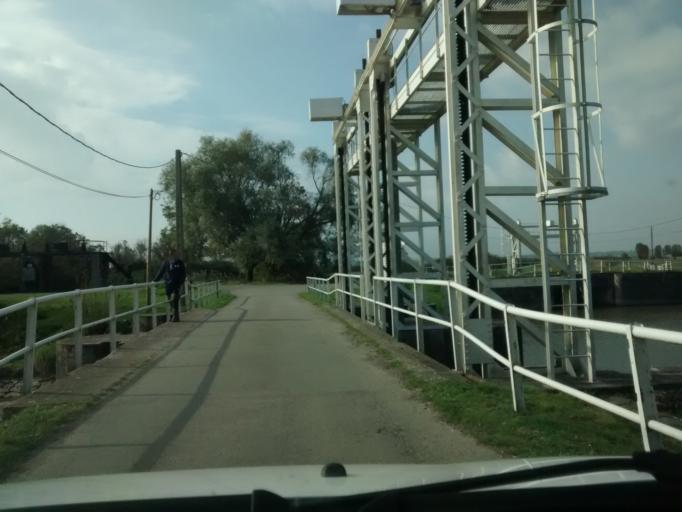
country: FR
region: Pays de la Loire
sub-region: Departement de la Loire-Atlantique
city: Vue
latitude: 47.2384
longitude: -1.8716
